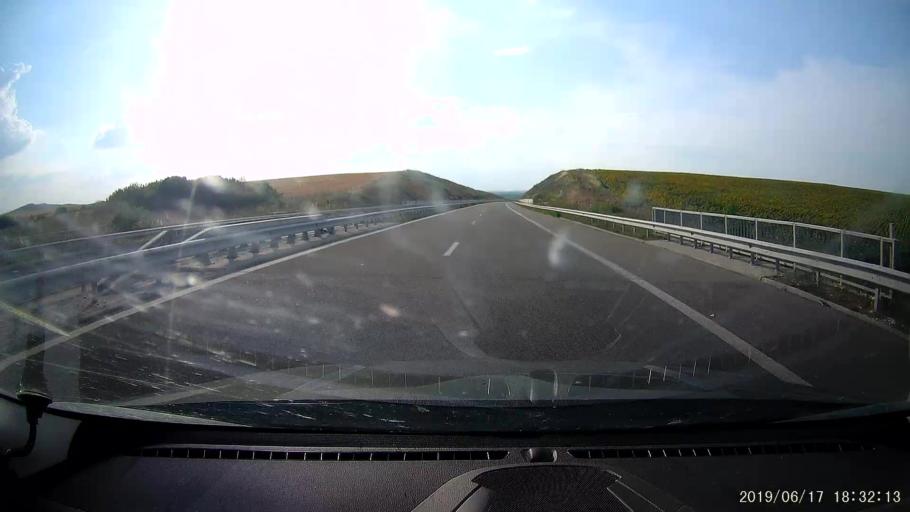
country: BG
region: Khaskovo
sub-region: Obshtina Dimitrovgrad
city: Dimitrovgrad
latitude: 42.0563
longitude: 25.4844
